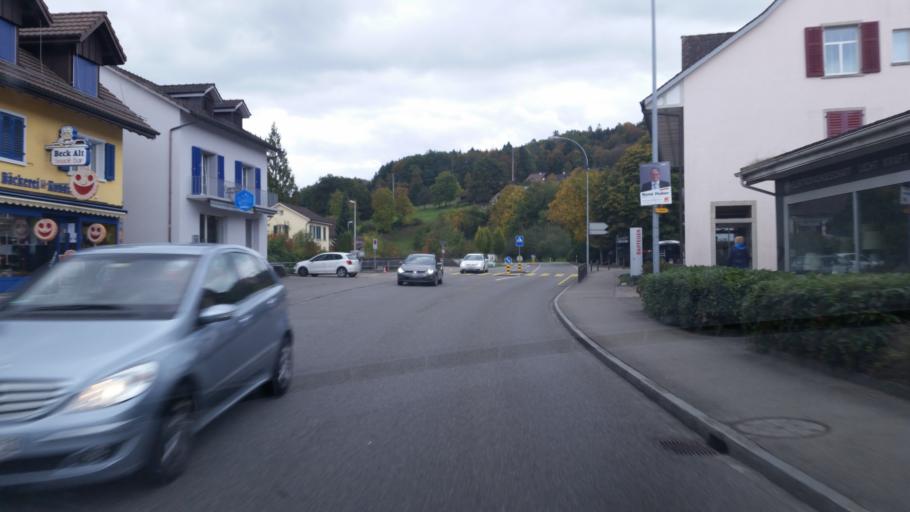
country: CH
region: Aargau
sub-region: Bezirk Zurzach
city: Oberendingen
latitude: 47.5372
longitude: 8.2906
